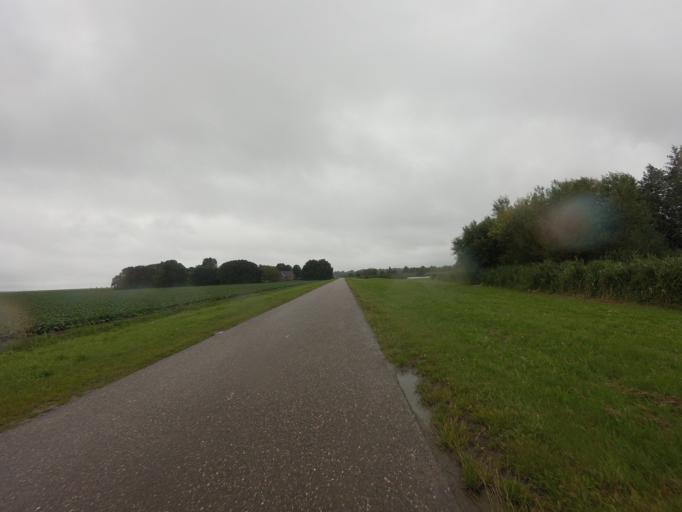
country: NL
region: North Holland
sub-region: Gemeente Huizen
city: Huizen
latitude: 52.3277
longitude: 5.2761
